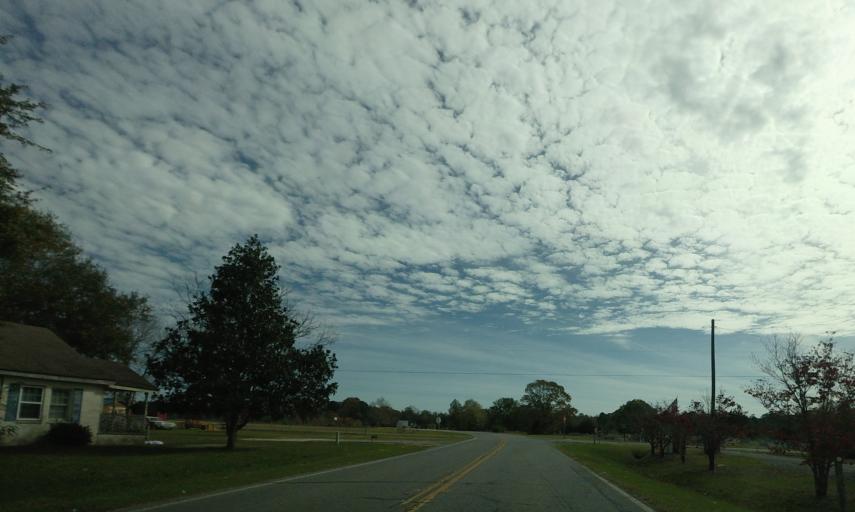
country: US
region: Georgia
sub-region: Bleckley County
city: Cochran
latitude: 32.3956
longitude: -83.2828
